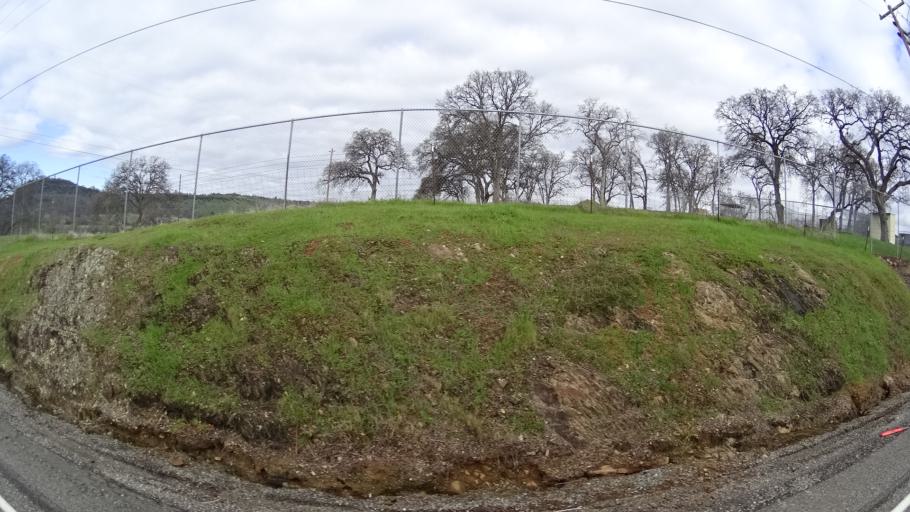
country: US
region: California
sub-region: Butte County
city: Paradise
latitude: 39.6567
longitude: -121.5764
